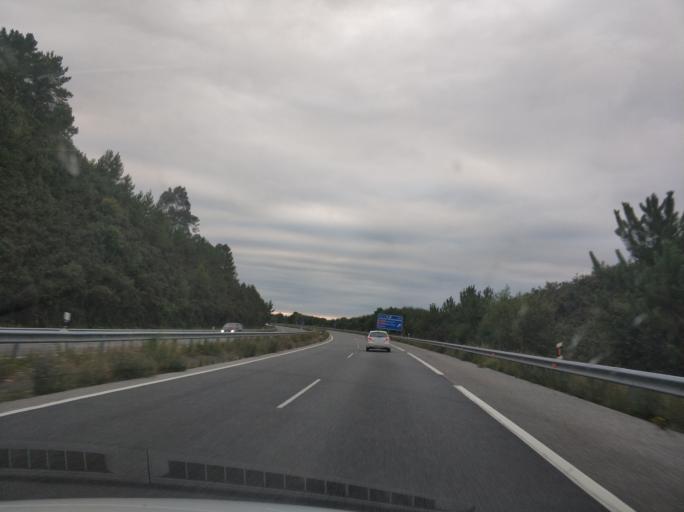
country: ES
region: Asturias
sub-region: Province of Asturias
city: Tineo
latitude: 43.5446
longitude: -6.4341
